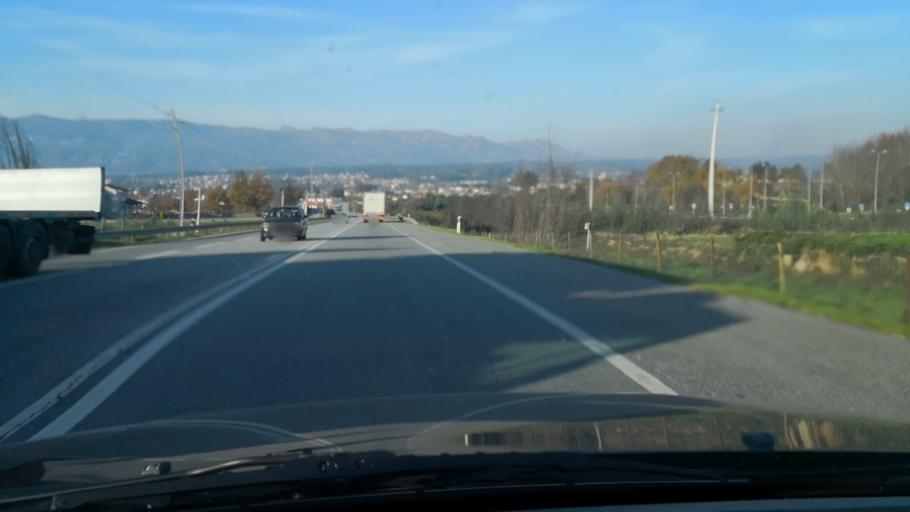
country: PT
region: Viseu
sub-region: Concelho de Tondela
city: Tondela
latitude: 40.5054
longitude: -8.0845
